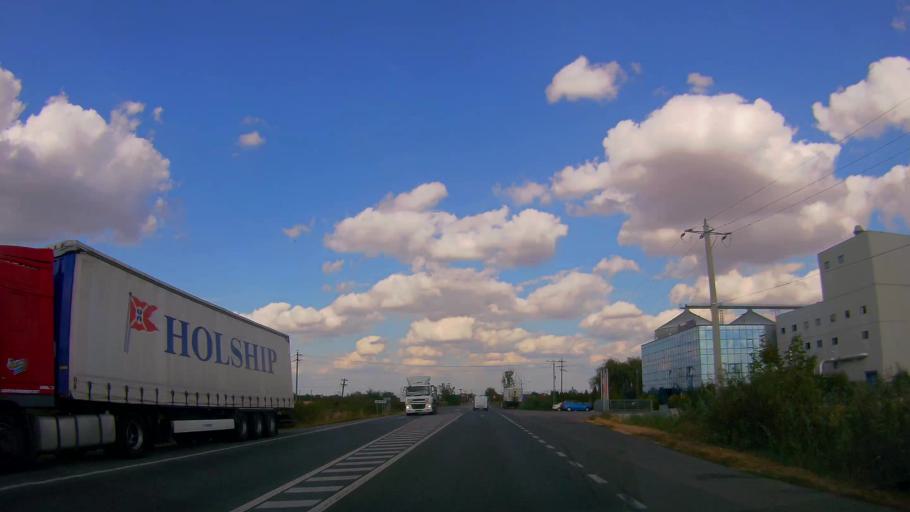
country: RO
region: Satu Mare
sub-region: Comuna Botiz
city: Botiz
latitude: 47.8205
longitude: 22.9375
